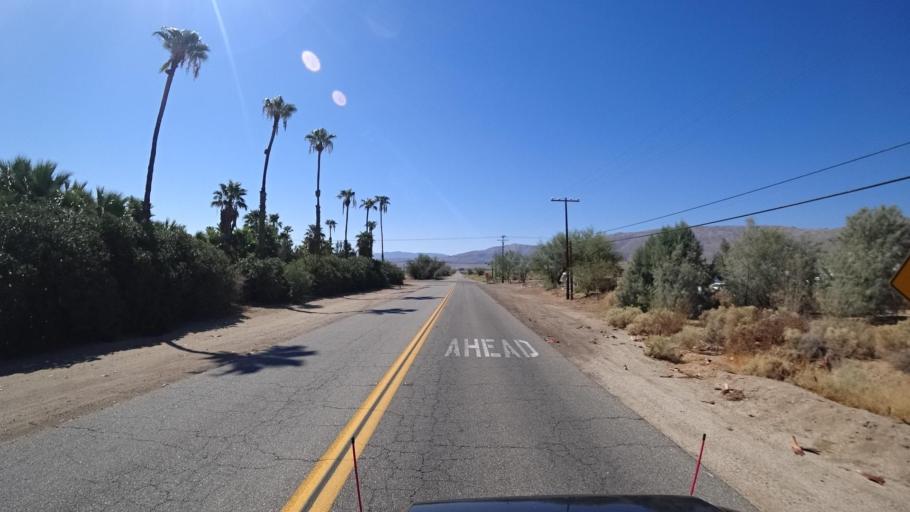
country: US
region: California
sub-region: San Diego County
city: Borrego Springs
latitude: 33.2578
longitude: -116.3660
